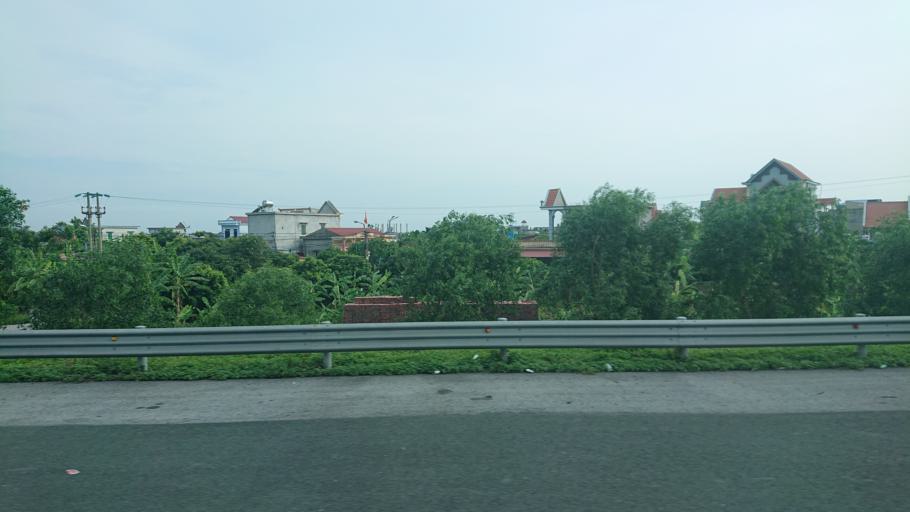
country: VN
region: Hai Phong
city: An Lao
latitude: 20.8133
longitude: 106.4984
